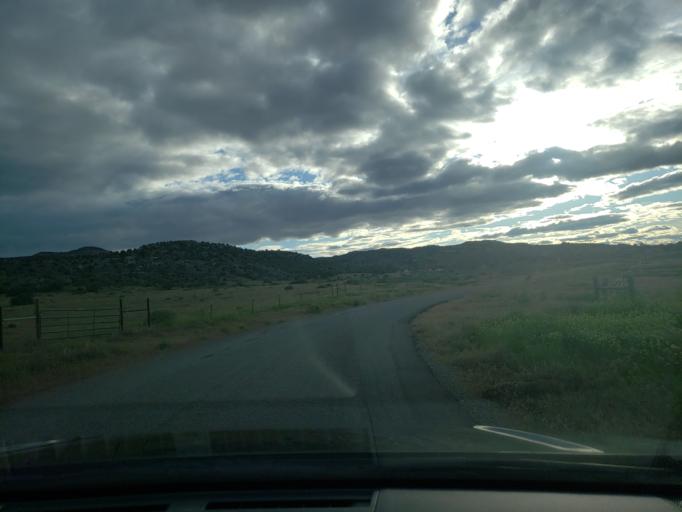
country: US
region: Colorado
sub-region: Mesa County
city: Fruita
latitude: 39.1400
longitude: -108.7513
